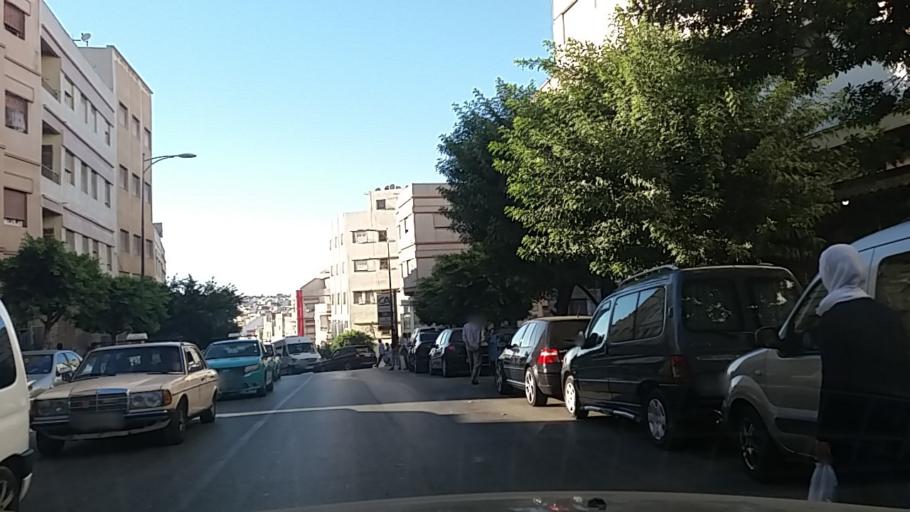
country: MA
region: Tanger-Tetouan
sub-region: Tanger-Assilah
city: Tangier
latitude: 35.7561
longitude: -5.8208
